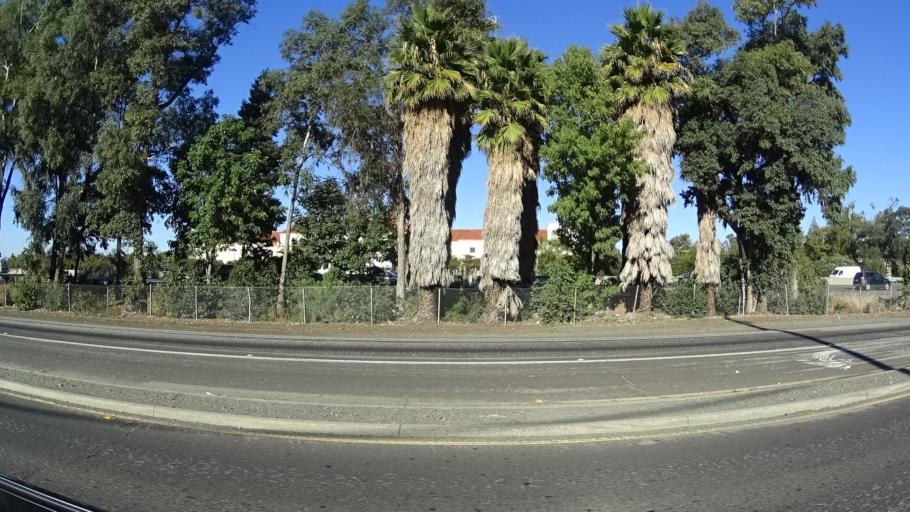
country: US
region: California
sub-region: Santa Clara County
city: San Jose
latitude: 37.3703
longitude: -121.9138
